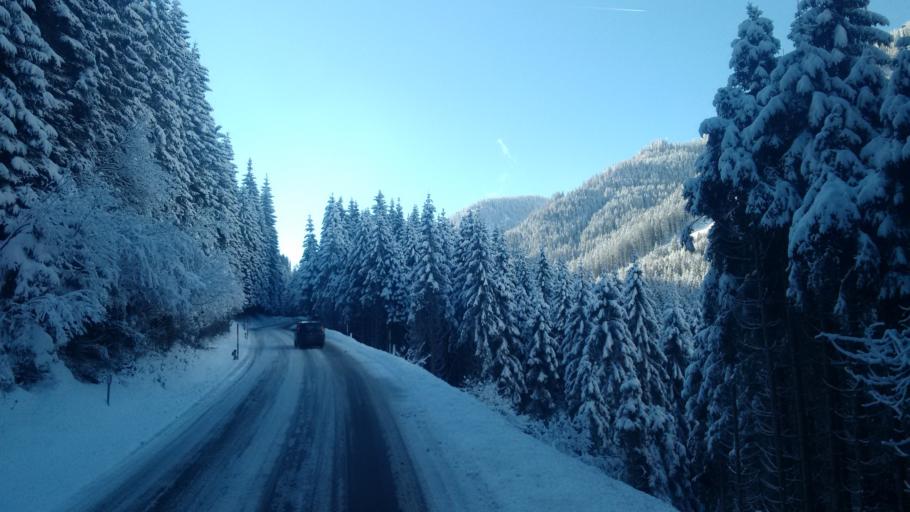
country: AT
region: Salzburg
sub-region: Politischer Bezirk Sankt Johann im Pongau
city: Flachau
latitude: 47.3231
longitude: 13.4455
